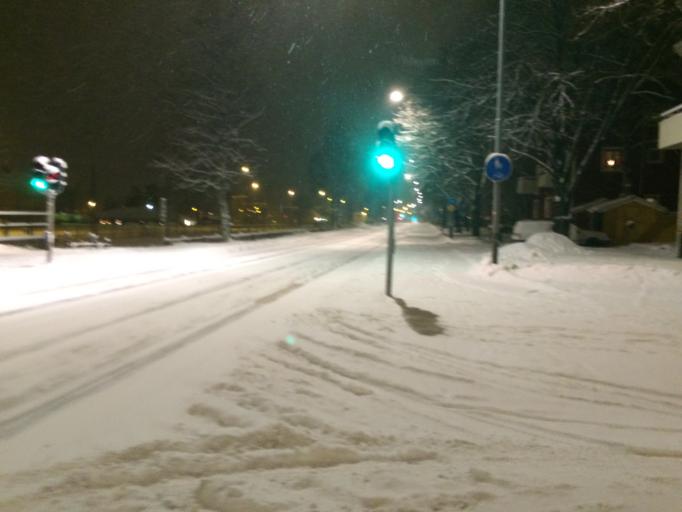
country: SE
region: Vaesterbotten
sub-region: Skelleftea Kommun
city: Skelleftea
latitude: 64.7540
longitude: 20.9539
